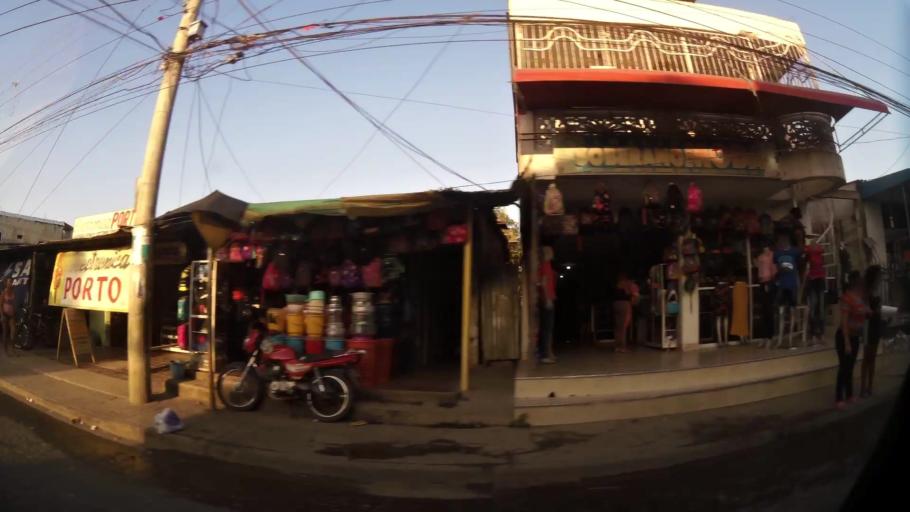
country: CO
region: Bolivar
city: Cartagena
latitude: 10.4111
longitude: -75.4566
